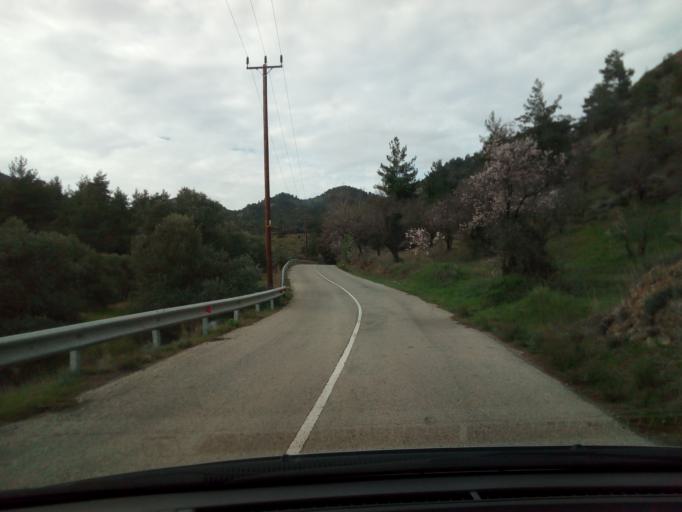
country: CY
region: Lefkosia
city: Klirou
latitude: 34.9789
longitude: 33.1838
